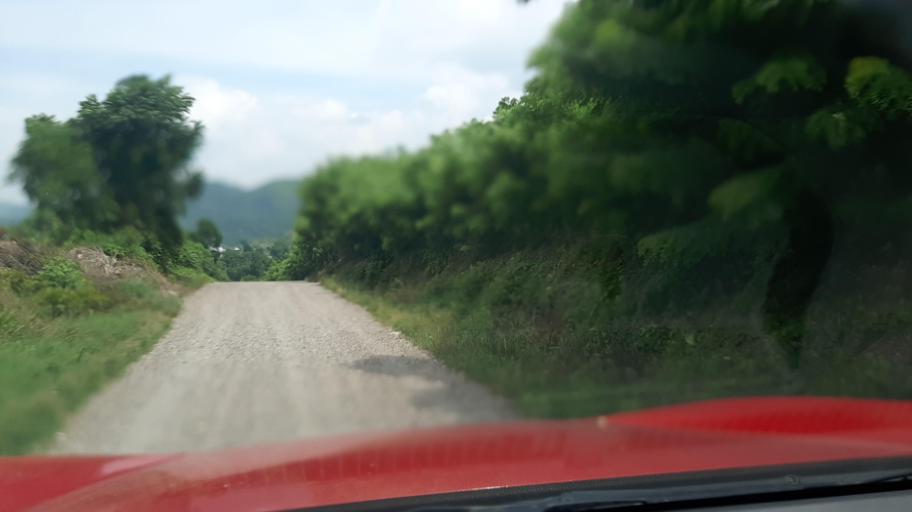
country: MX
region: Veracruz
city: Gutierrez Zamora
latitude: 20.4596
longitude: -97.1827
